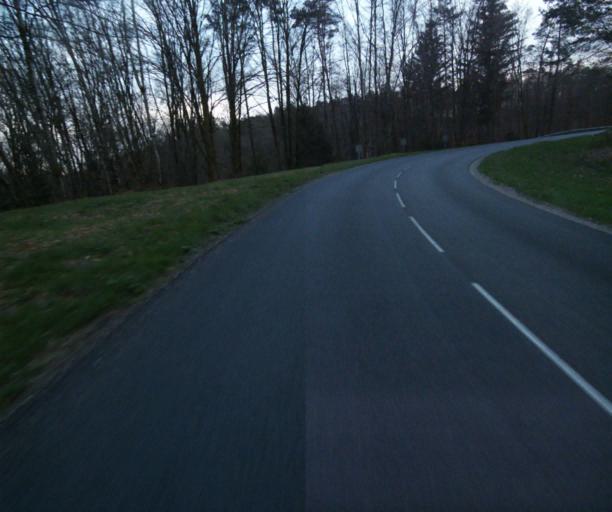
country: FR
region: Limousin
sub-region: Departement de la Correze
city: Correze
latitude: 45.3527
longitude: 1.8768
